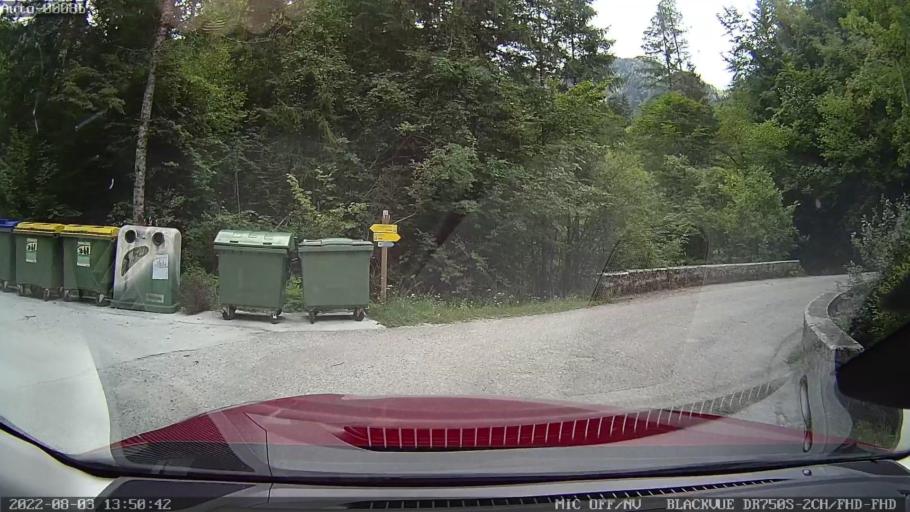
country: SI
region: Bovec
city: Bovec
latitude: 46.3378
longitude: 13.6856
